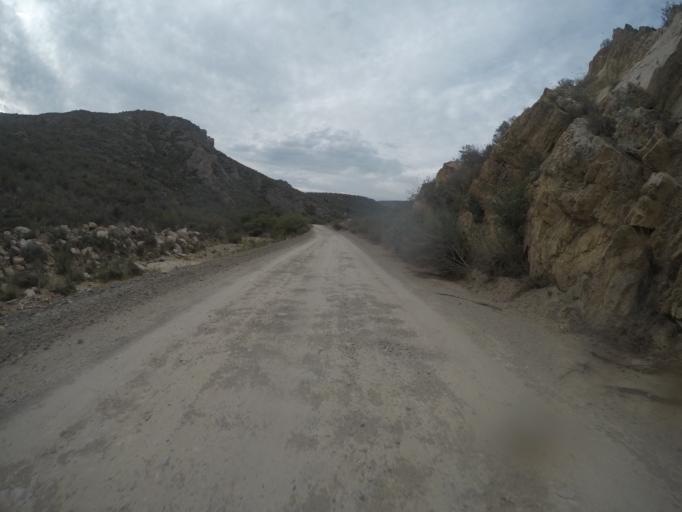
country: ZA
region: Eastern Cape
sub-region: Cacadu District Municipality
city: Willowmore
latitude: -33.5038
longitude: 23.6354
